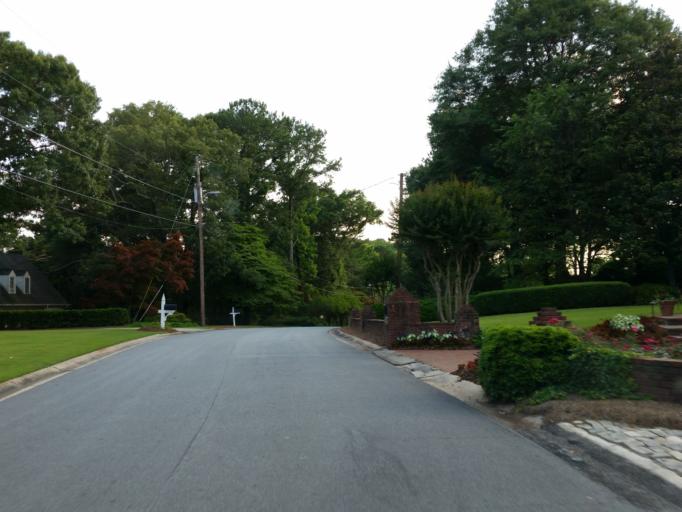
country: US
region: Georgia
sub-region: Cobb County
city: Vinings
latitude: 33.8661
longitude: -84.4615
